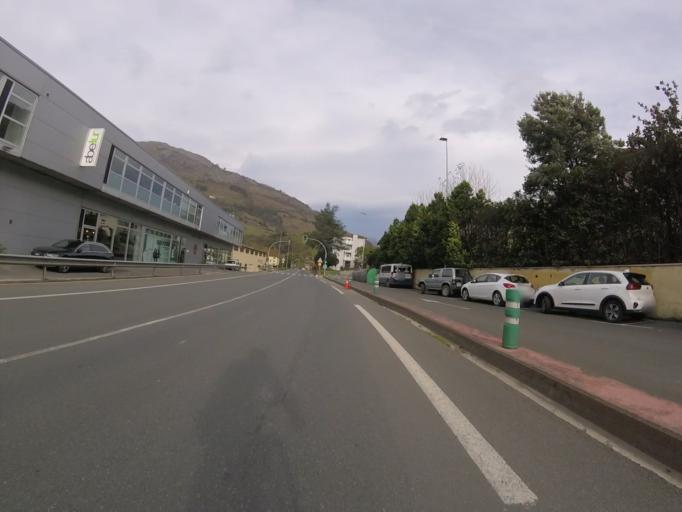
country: ES
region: Basque Country
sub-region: Provincia de Guipuzcoa
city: Azpeitia
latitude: 43.1841
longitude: -2.2601
